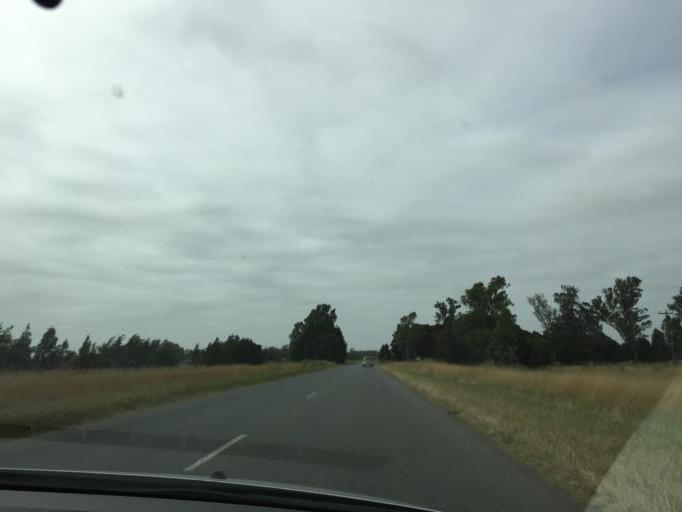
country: AR
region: Buenos Aires
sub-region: Partido de Las Flores
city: Las Flores
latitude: -36.2011
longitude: -59.0515
